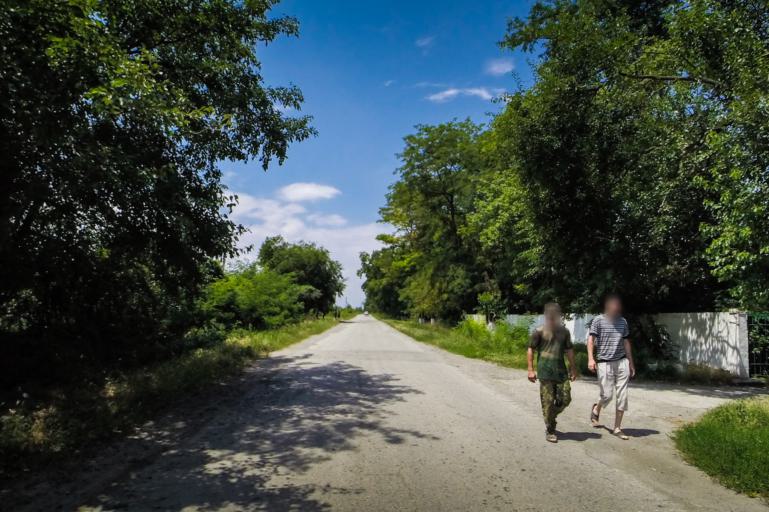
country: RU
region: Kabardino-Balkariya
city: Altud
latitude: 43.7571
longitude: 43.8813
